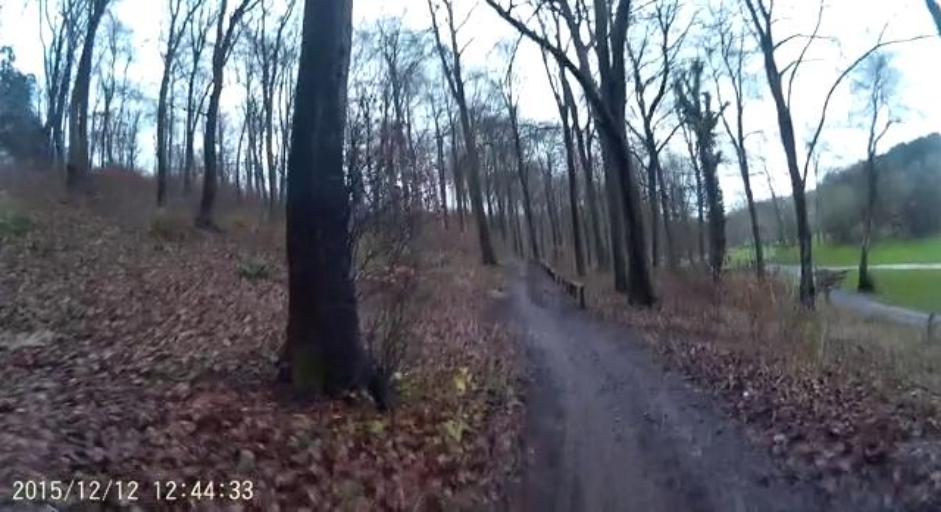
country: GB
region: England
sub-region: Hampshire
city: Petersfield
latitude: 50.9608
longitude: -0.9776
